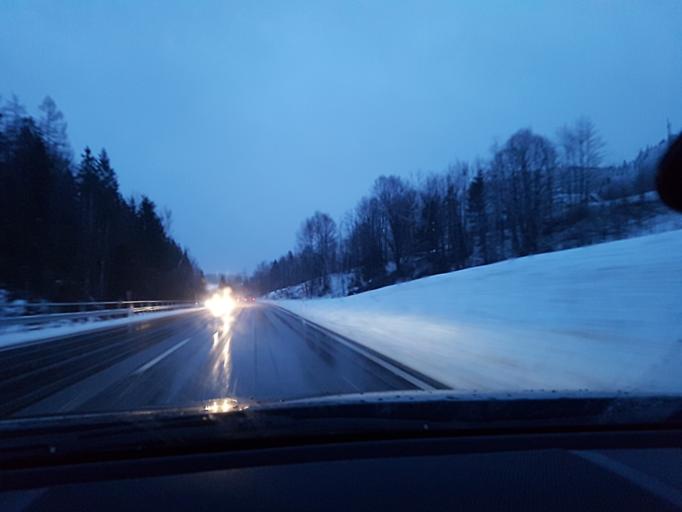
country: AT
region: Salzburg
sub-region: Politischer Bezirk Salzburg-Umgebung
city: Sankt Gilgen
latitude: 47.7879
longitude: 13.3383
